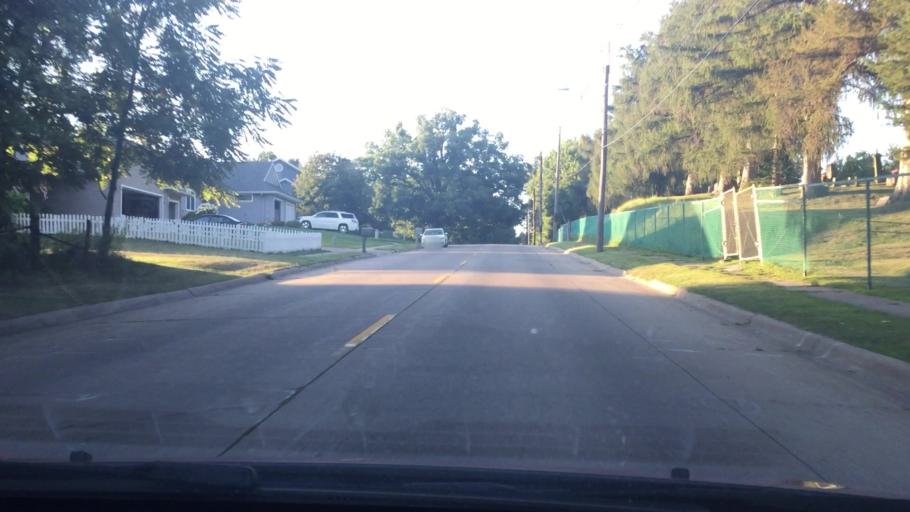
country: US
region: Iowa
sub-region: Muscatine County
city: Muscatine
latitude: 41.4248
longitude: -91.0650
